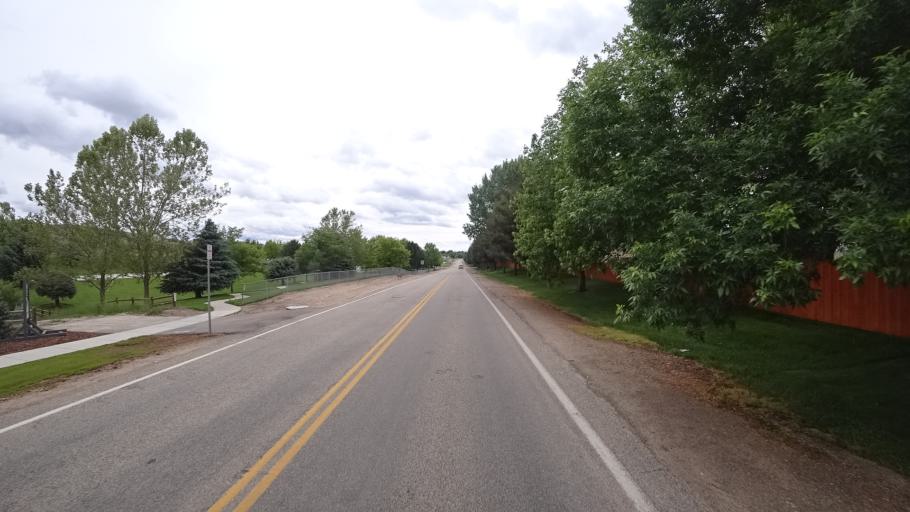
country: US
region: Idaho
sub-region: Ada County
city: Eagle
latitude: 43.7139
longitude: -116.3167
